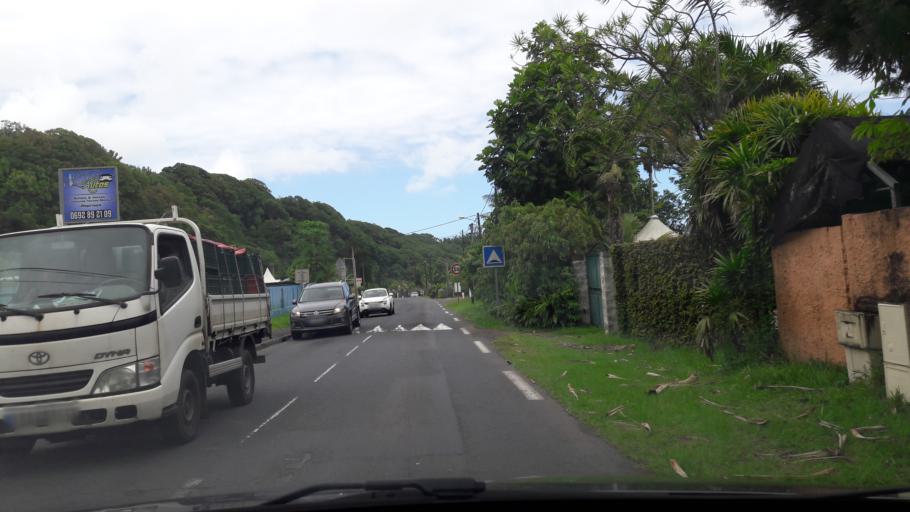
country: RE
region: Reunion
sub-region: Reunion
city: Saint-Andre
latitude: -20.9819
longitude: 55.6301
